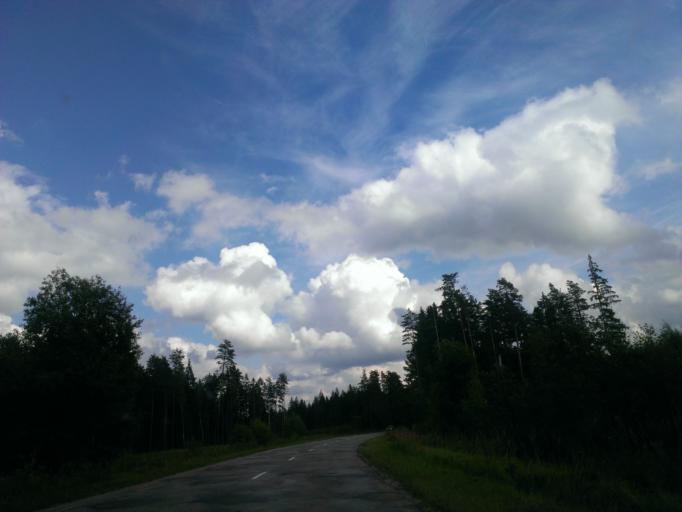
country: LV
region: Ropazu
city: Ropazi
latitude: 57.0248
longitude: 24.6309
